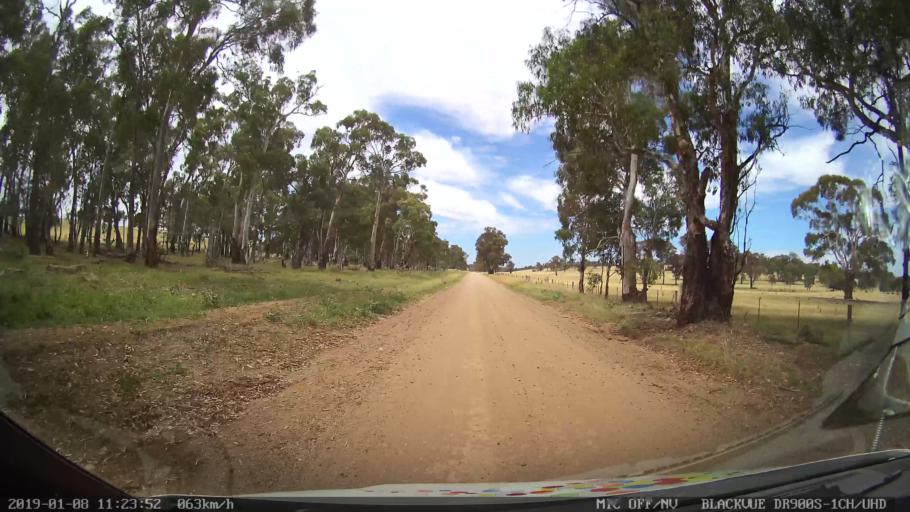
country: AU
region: New South Wales
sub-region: Guyra
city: Guyra
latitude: -30.2592
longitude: 151.5585
